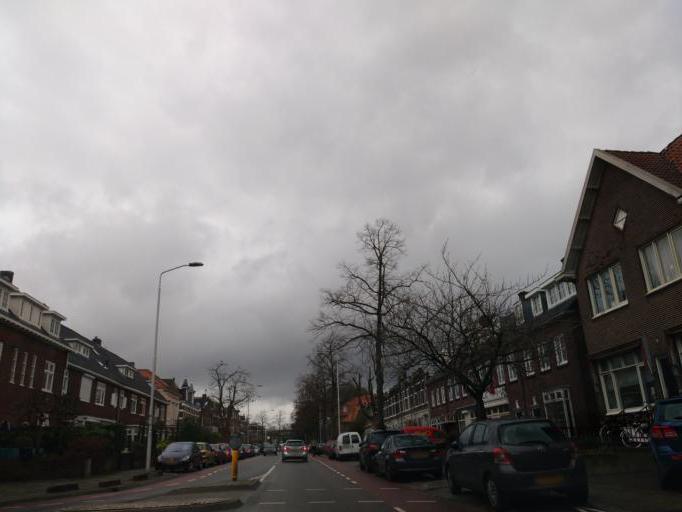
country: NL
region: Gelderland
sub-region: Gemeente Groesbeek
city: Berg en Dal
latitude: 51.8359
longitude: 5.8861
